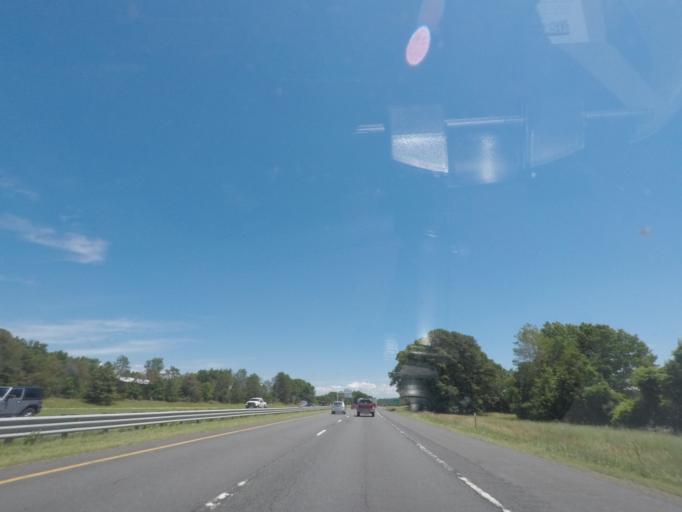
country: US
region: Massachusetts
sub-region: Hampden County
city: Westfield
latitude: 42.1430
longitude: -72.7243
